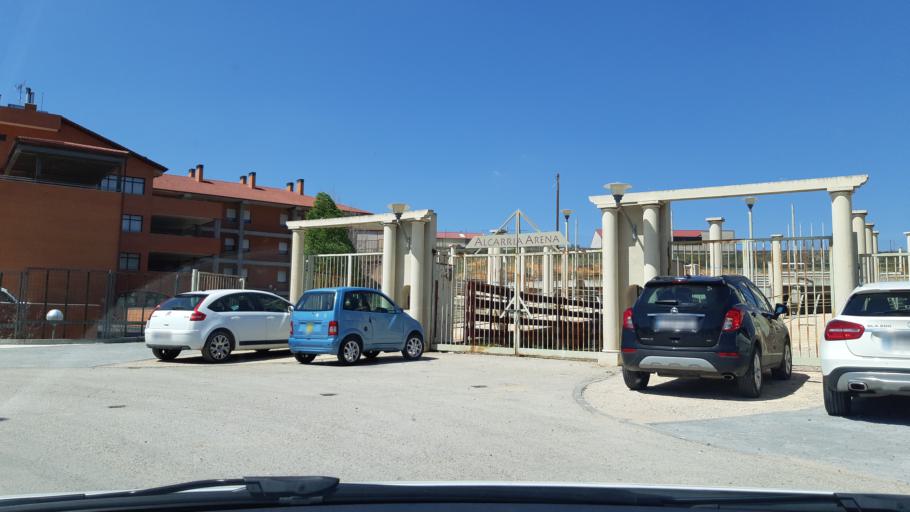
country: ES
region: Castille-La Mancha
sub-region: Provincia de Guadalajara
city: Cifuentes
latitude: 40.7880
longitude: -2.6203
